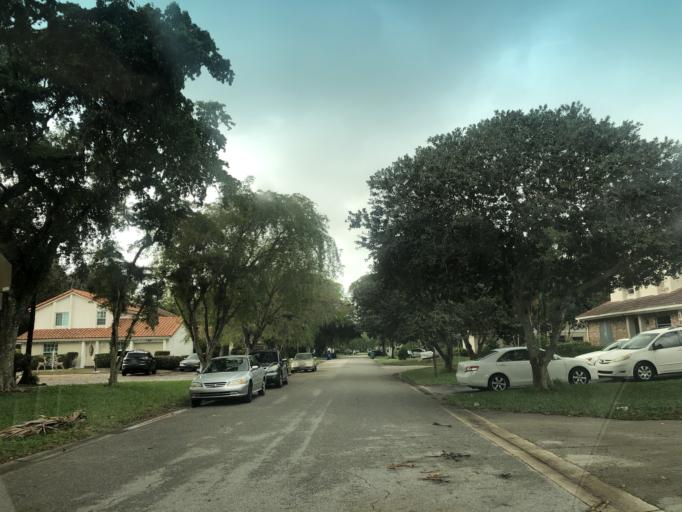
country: US
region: Florida
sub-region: Broward County
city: Tamarac
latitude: 26.2466
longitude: -80.2449
